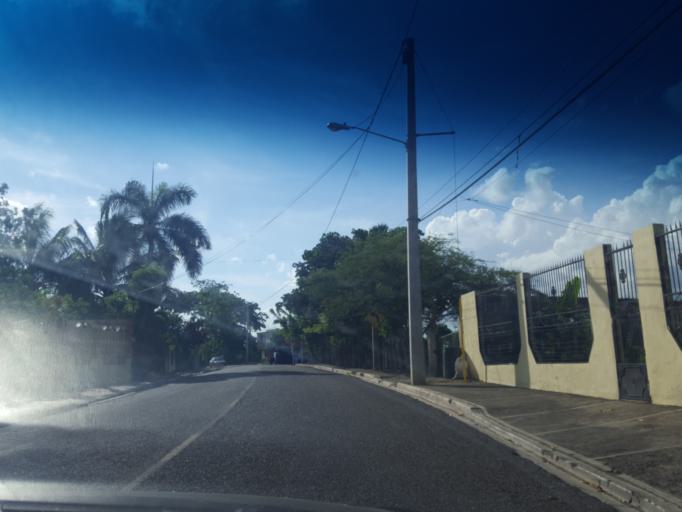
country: DO
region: Santiago
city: Licey al Medio
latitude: 19.3788
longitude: -70.6123
